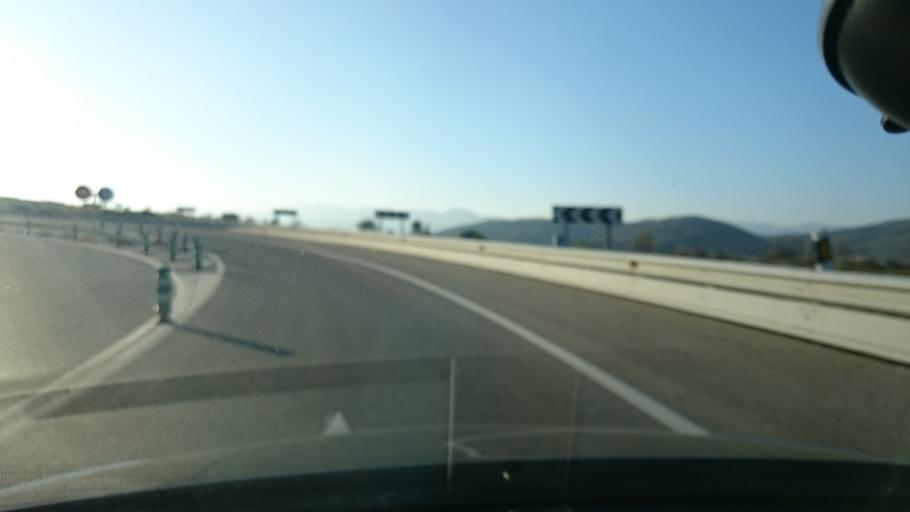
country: ES
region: Castille and Leon
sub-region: Provincia de Leon
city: Villafranca del Bierzo
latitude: 42.5955
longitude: -6.8022
